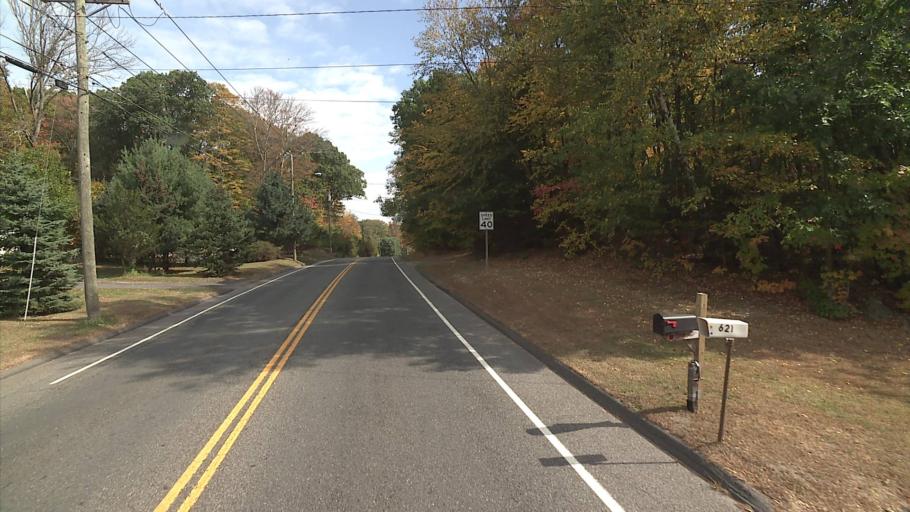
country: US
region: Connecticut
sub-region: Litchfield County
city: Plymouth
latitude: 41.6726
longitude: -73.0463
